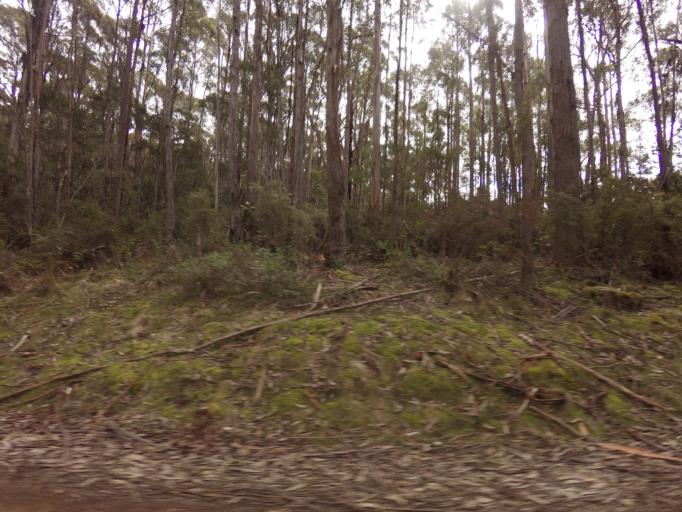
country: AU
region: Tasmania
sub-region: Huon Valley
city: Geeveston
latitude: -43.4222
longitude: 147.0111
